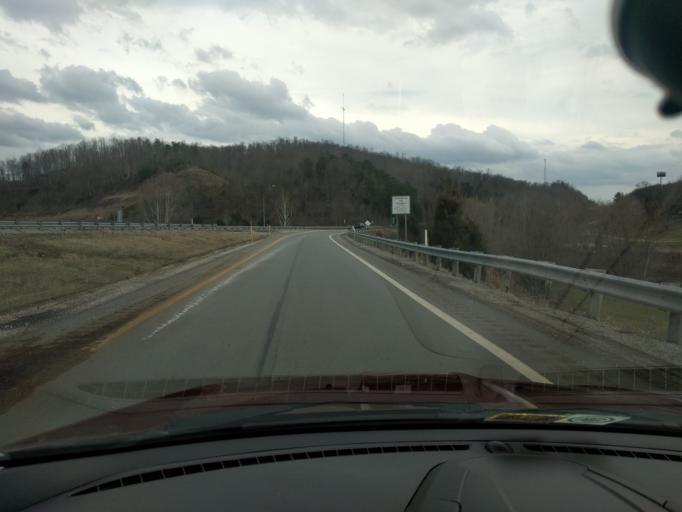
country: US
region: West Virginia
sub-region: Jackson County
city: Ripley
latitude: 38.8195
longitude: -81.7286
